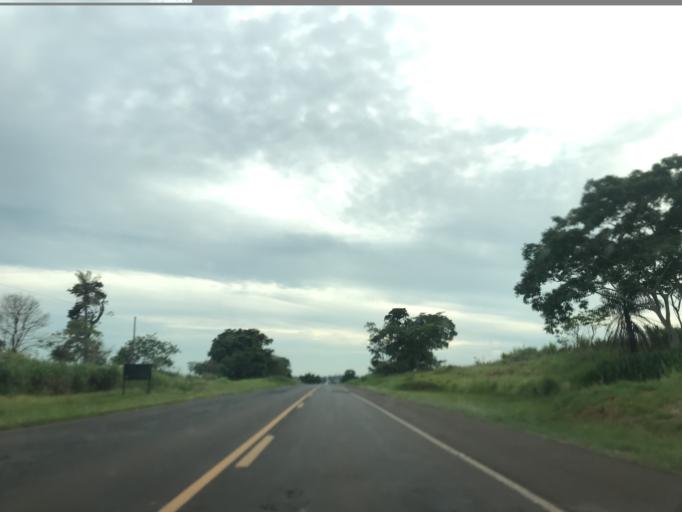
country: BR
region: Sao Paulo
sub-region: Birigui
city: Birigui
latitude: -21.5671
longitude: -50.4194
